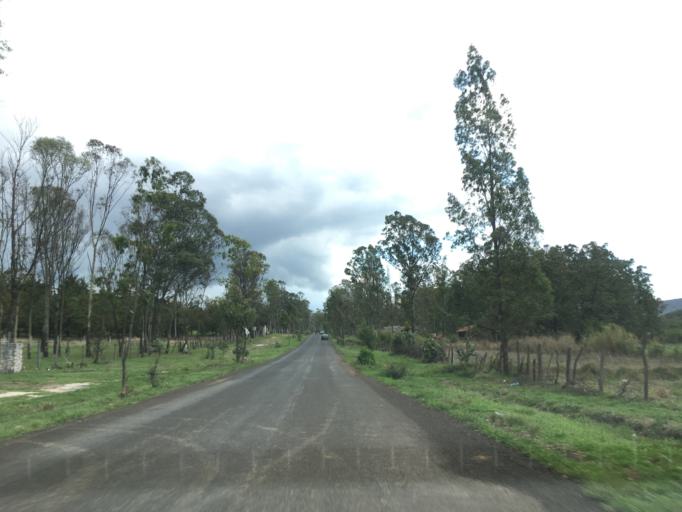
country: MX
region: Michoacan
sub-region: Morelia
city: La Mintzita (Piedra Dura)
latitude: 19.5697
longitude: -101.2737
